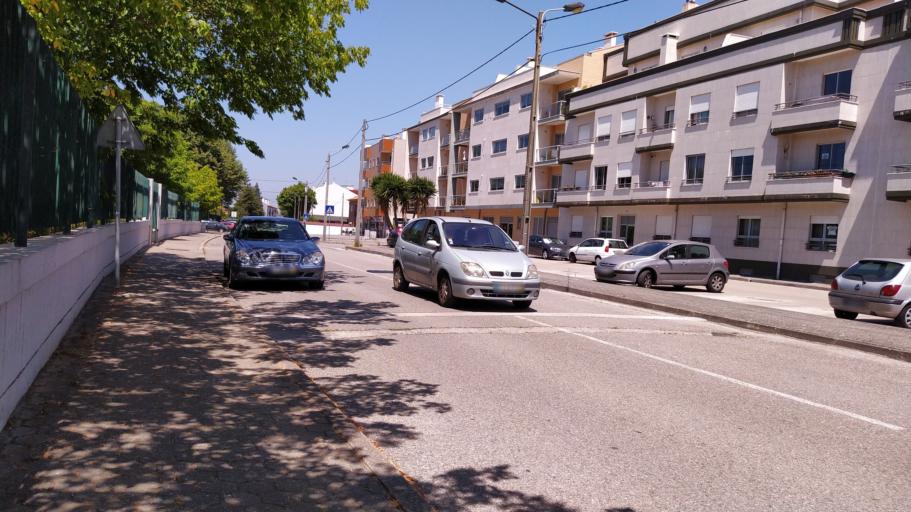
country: PT
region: Aveiro
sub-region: Aveiro
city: Aveiro
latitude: 40.6451
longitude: -8.6312
